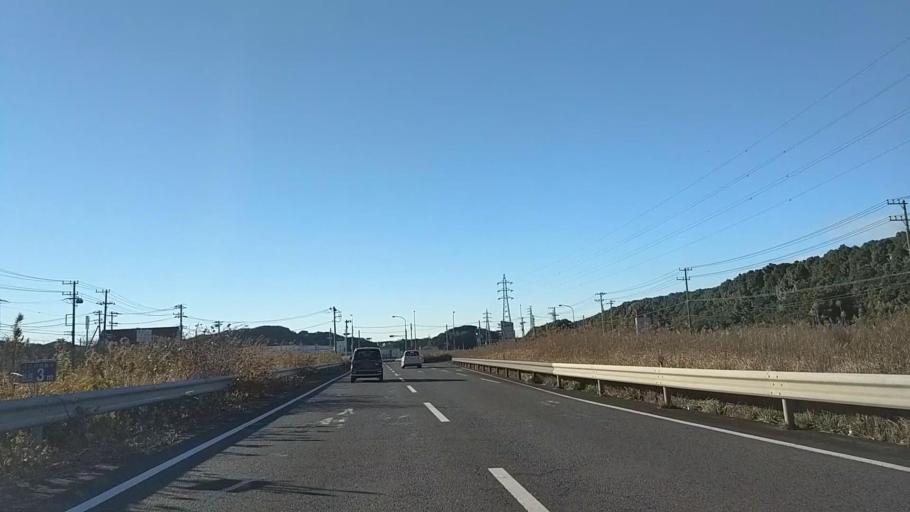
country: JP
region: Chiba
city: Kisarazu
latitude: 35.3642
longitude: 139.9117
